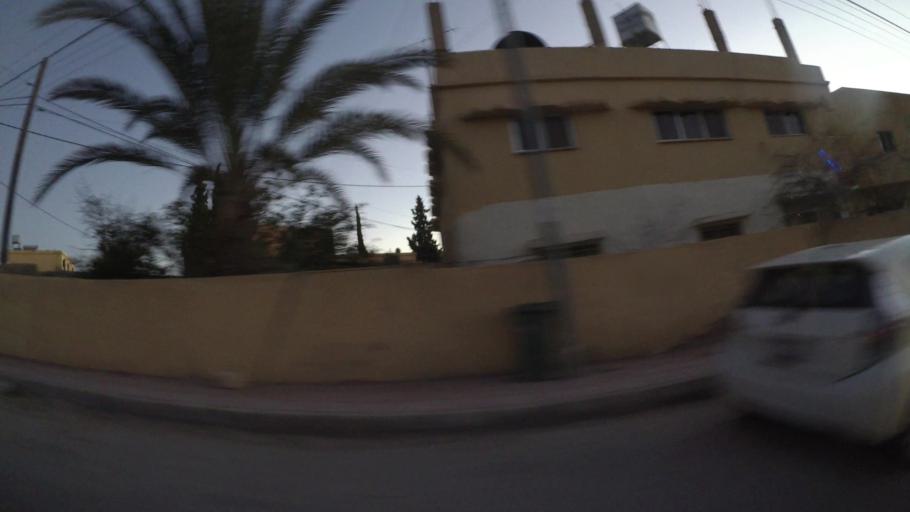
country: JO
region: Ma'an
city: Petra
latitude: 30.3248
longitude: 35.4791
